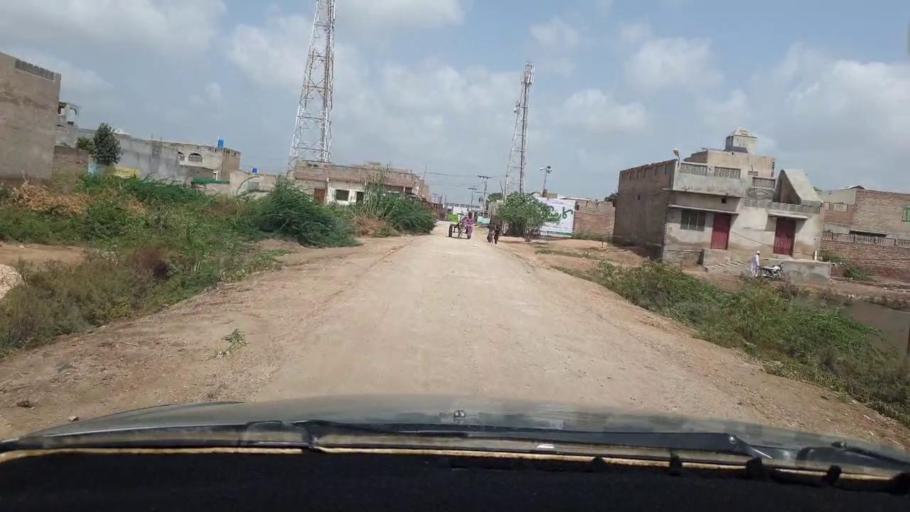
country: PK
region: Sindh
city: Tando Bago
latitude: 24.7612
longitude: 69.1909
